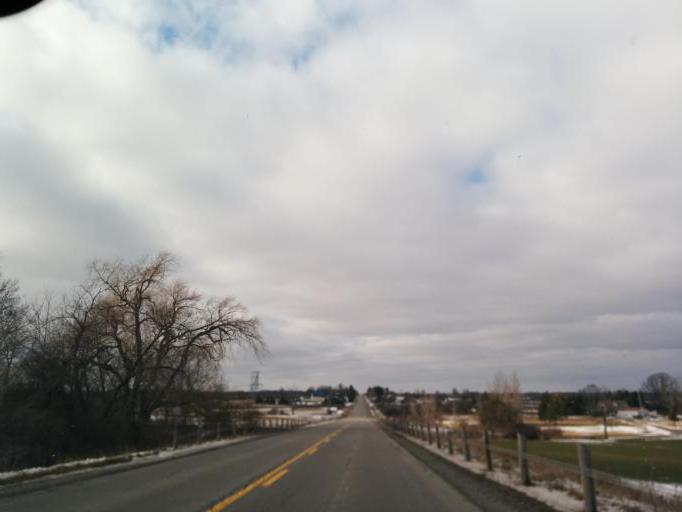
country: CA
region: Ontario
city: Brantford
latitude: 42.9746
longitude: -80.0859
